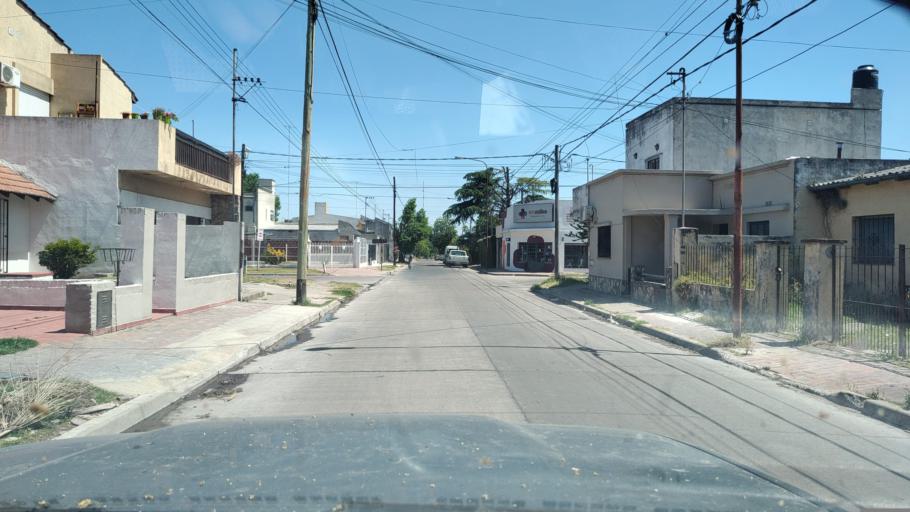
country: AR
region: Buenos Aires
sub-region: Partido de Lujan
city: Lujan
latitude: -34.5809
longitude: -59.1098
